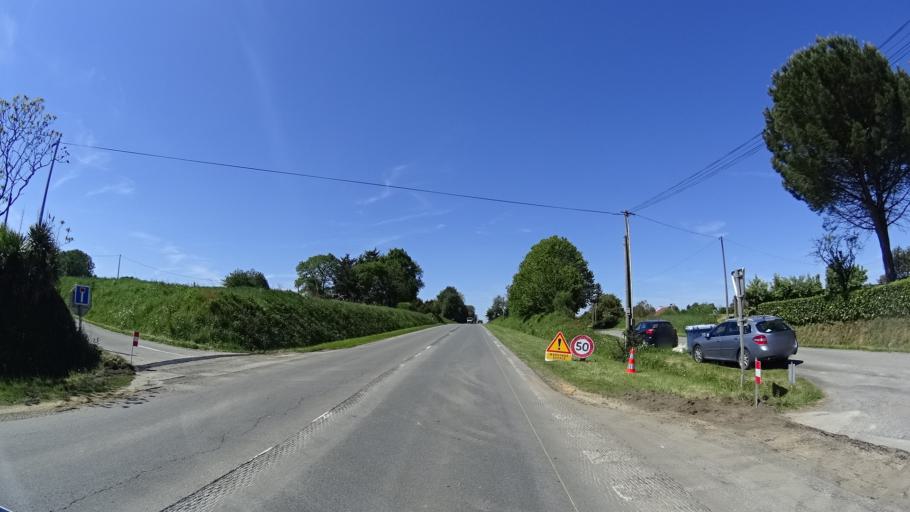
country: FR
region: Brittany
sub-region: Departement d'Ille-et-Vilaine
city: Melesse
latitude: 48.2048
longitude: -1.6961
